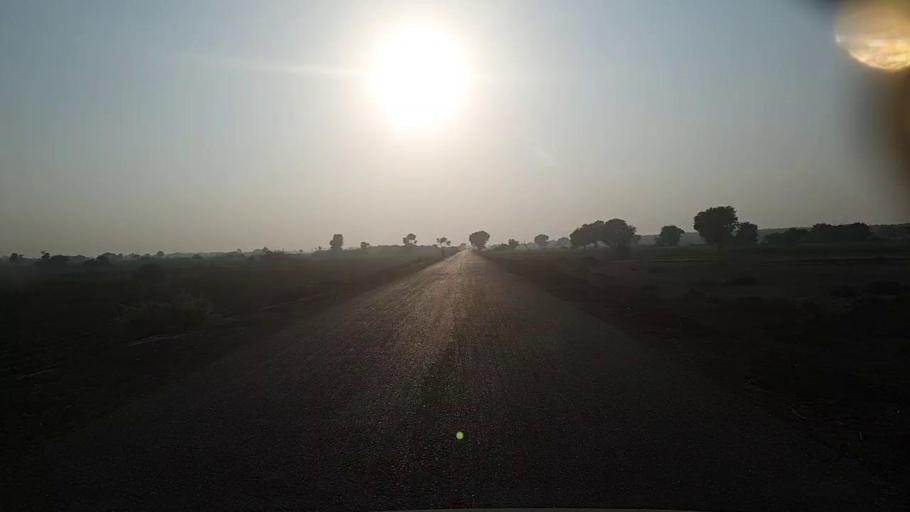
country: PK
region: Sindh
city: Pad Idan
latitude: 26.7135
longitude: 68.3971
